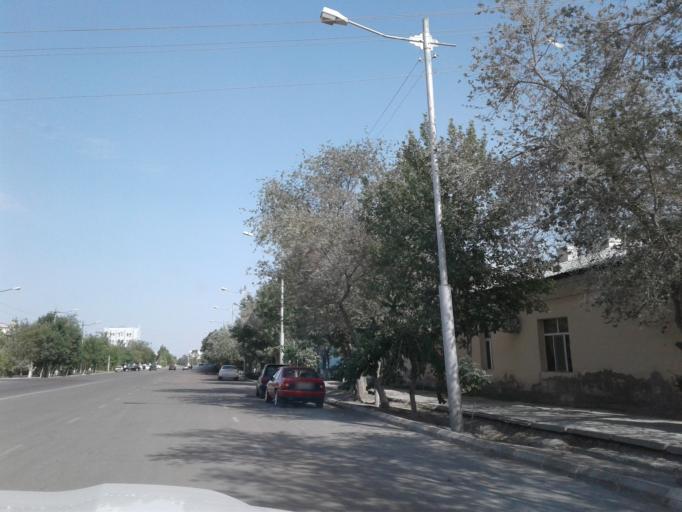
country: TM
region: Dasoguz
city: Dasoguz
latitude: 41.8315
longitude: 59.9581
